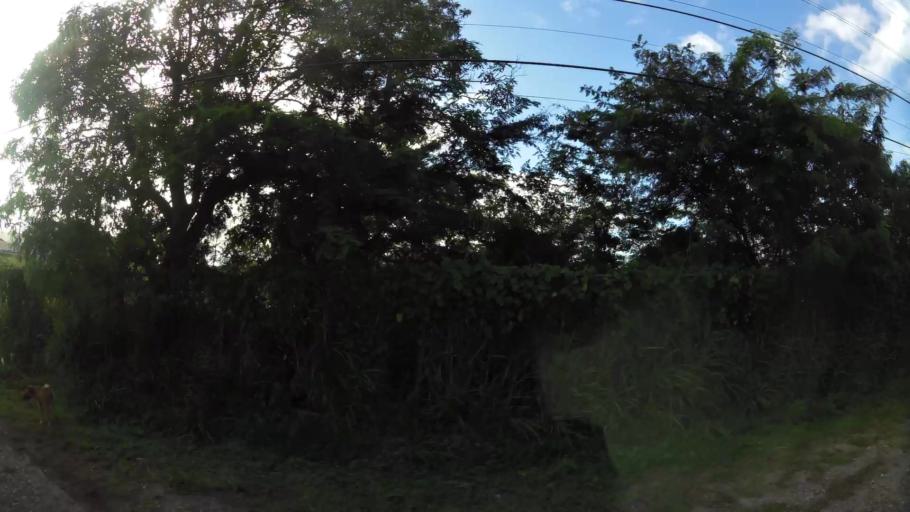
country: AG
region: Saint Peter
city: All Saints
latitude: 17.0617
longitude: -61.7948
